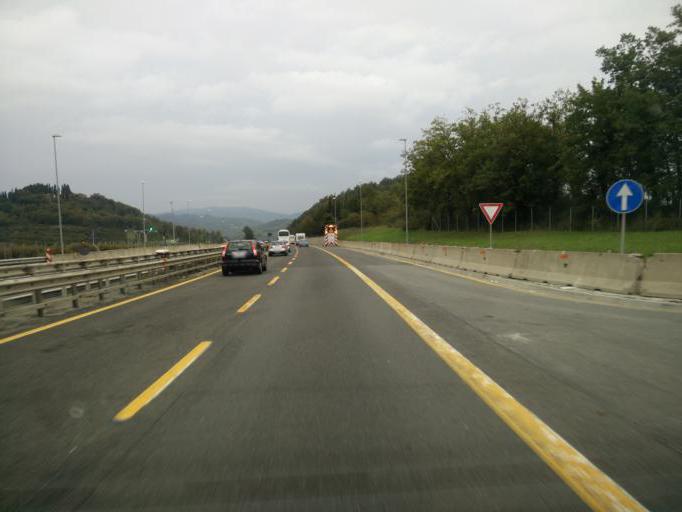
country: IT
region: Tuscany
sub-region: Province of Florence
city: Cavallina
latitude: 43.9655
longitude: 11.2115
